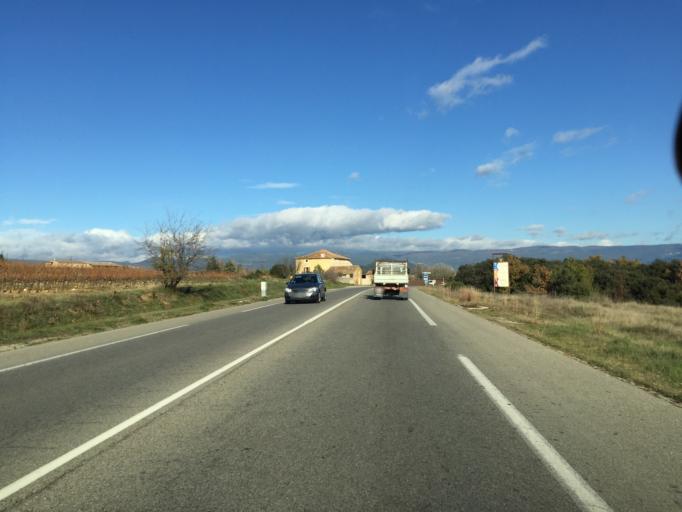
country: FR
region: Provence-Alpes-Cote d'Azur
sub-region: Departement du Vaucluse
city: Roussillon
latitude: 43.8690
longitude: 5.3204
